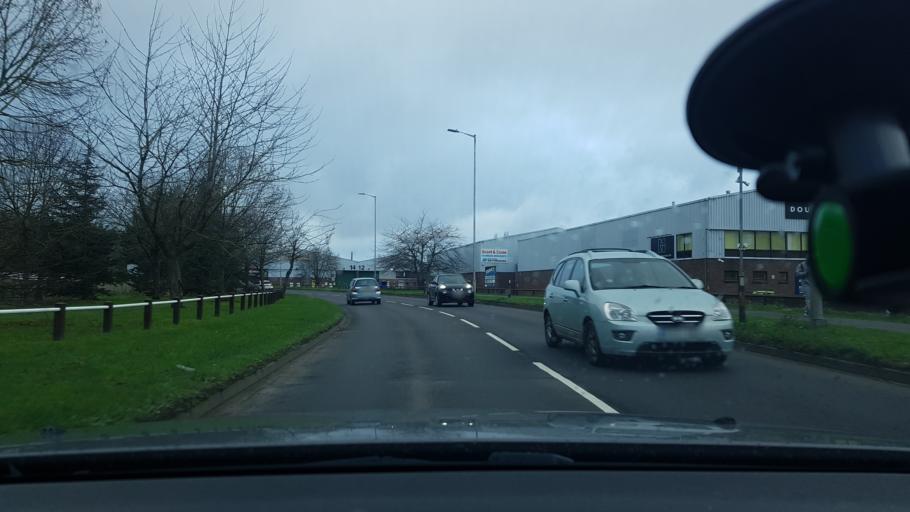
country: GB
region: England
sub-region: West Berkshire
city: Tilehurst
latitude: 51.4628
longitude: -1.0096
